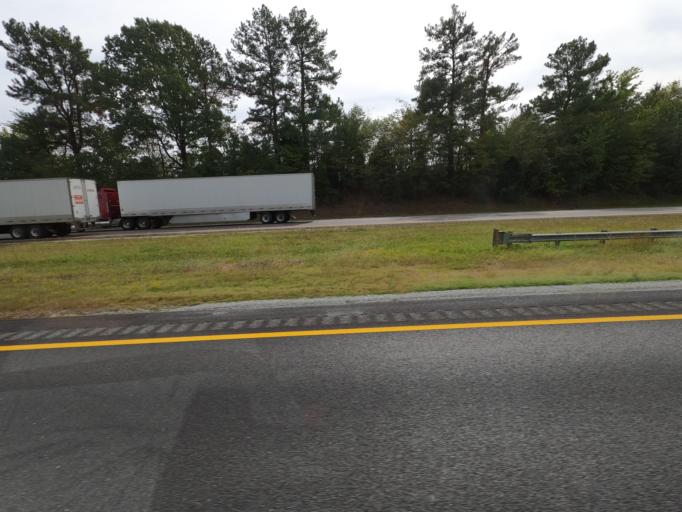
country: US
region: Tennessee
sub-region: Crockett County
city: Bells
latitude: 35.6229
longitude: -88.9824
